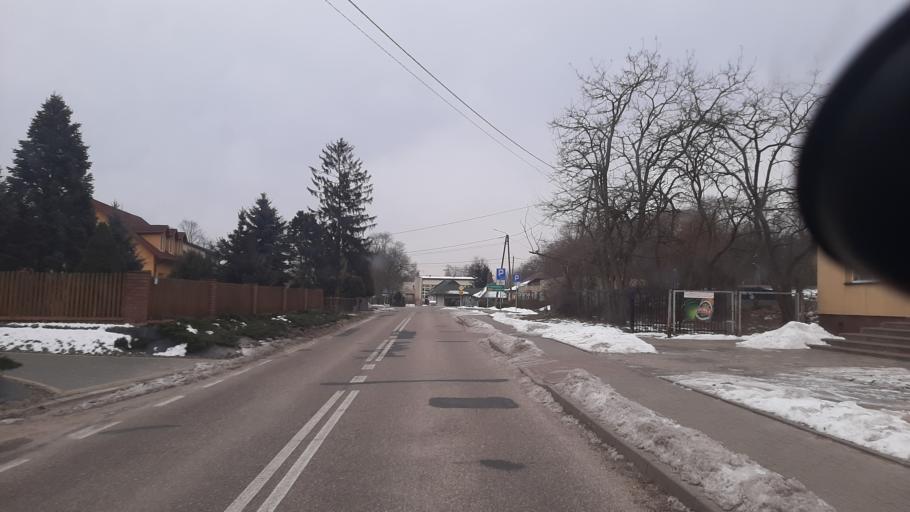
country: PL
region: Lublin Voivodeship
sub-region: Powiat lubartowski
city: Kamionka
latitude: 51.4464
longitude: 22.4237
